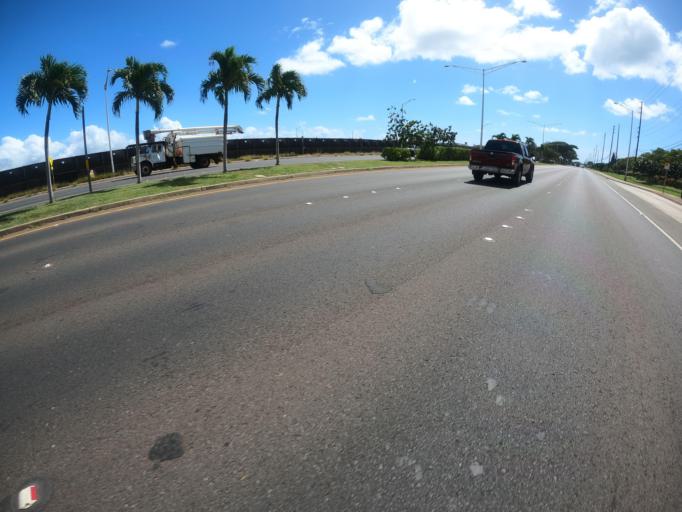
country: US
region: Hawaii
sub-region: Honolulu County
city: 'Ewa Gentry
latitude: 21.3470
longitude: -158.0268
